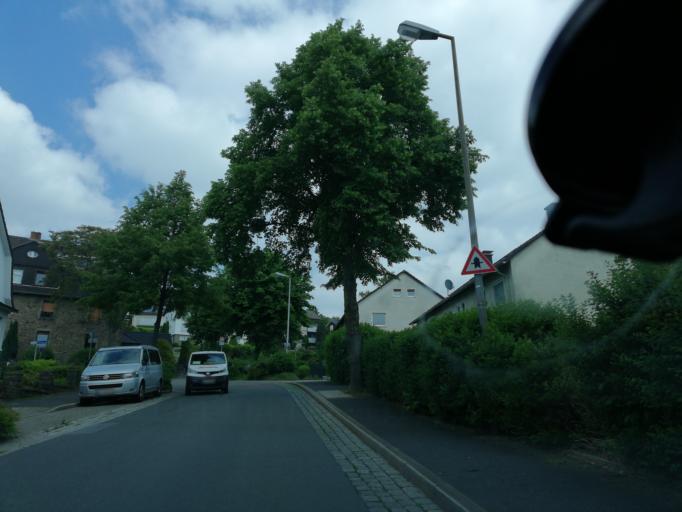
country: DE
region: North Rhine-Westphalia
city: Herdecke
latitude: 51.4044
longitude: 7.4299
